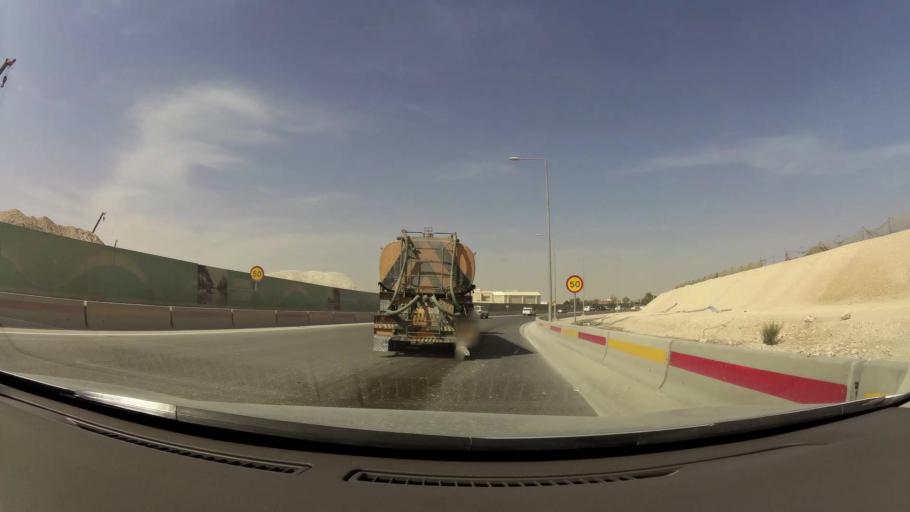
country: QA
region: Baladiyat ar Rayyan
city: Ar Rayyan
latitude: 25.3088
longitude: 51.4088
